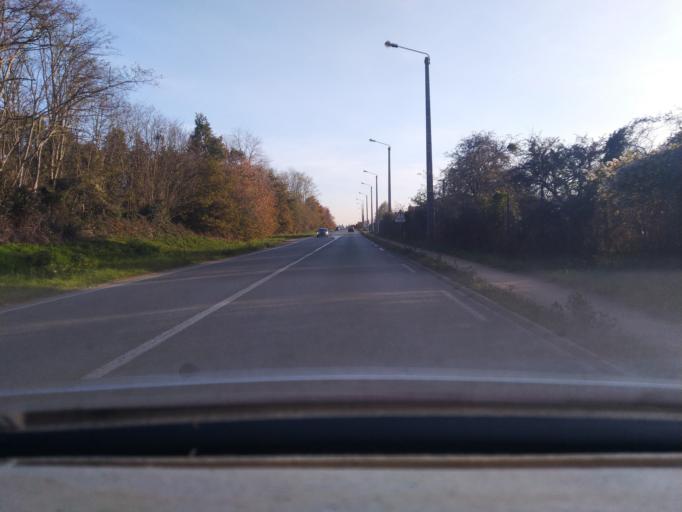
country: FR
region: Haute-Normandie
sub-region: Departement de la Seine-Maritime
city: Le Trait
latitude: 49.4658
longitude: 0.8191
